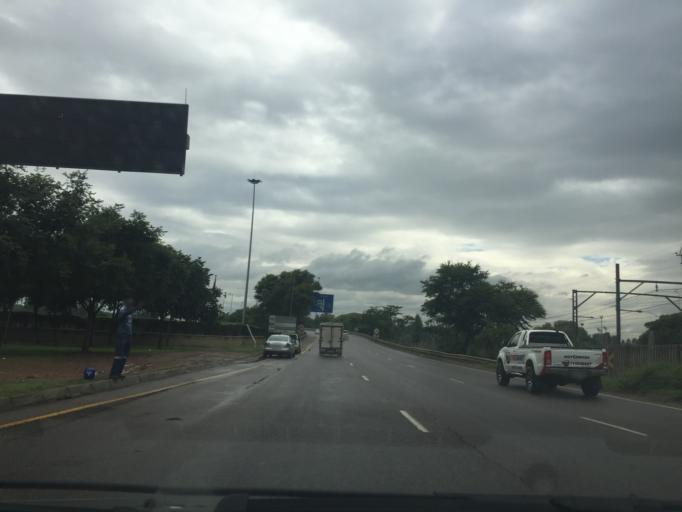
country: ZA
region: Gauteng
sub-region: City of Tshwane Metropolitan Municipality
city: Pretoria
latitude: -25.7444
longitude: 28.2467
